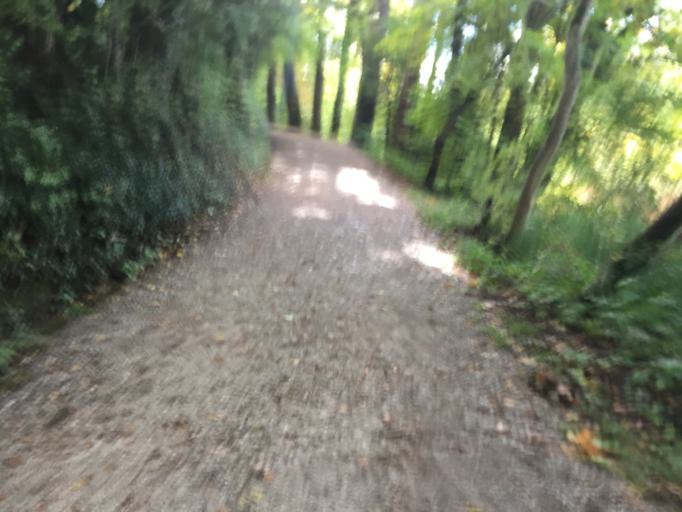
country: CH
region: Bern
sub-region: Bern-Mittelland District
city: Muri
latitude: 46.9216
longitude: 7.4969
